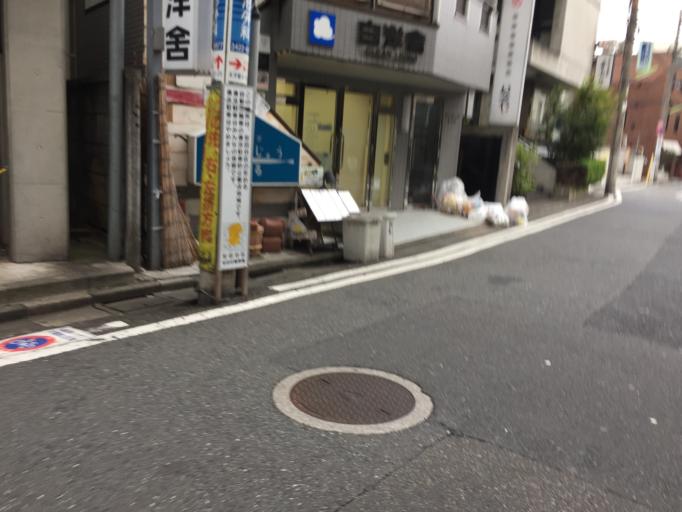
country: JP
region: Tokyo
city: Tokyo
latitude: 35.6445
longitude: 139.6700
